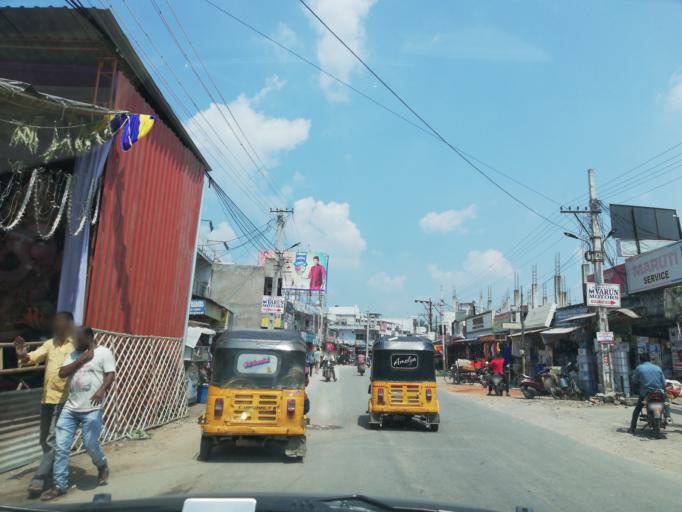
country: IN
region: Telangana
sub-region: Medak
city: Serilingampalle
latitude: 17.4913
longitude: 78.3167
